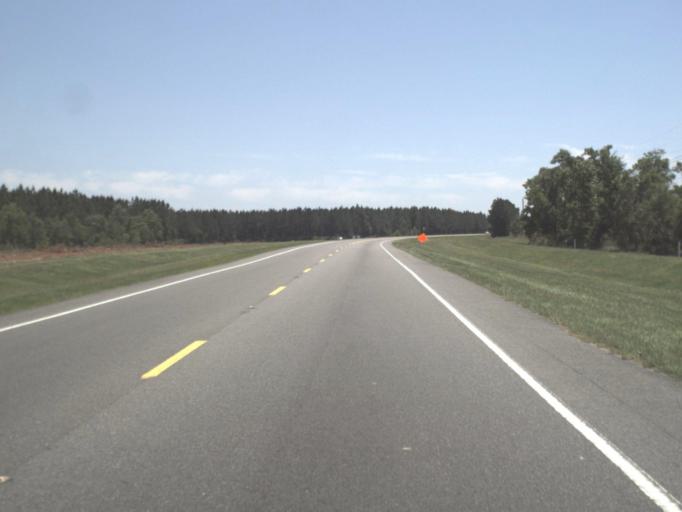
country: US
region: Florida
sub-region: Clay County
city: Lakeside
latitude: 30.1796
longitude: -81.8339
